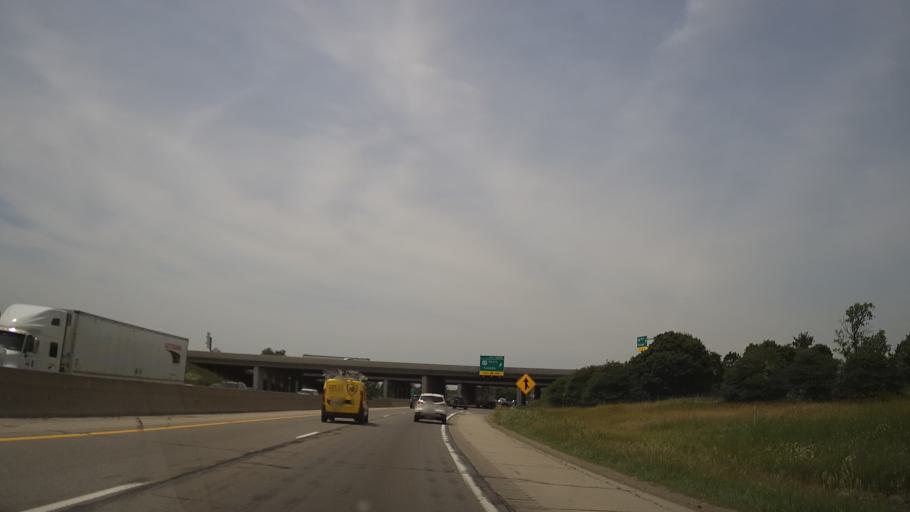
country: US
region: Michigan
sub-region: Washtenaw County
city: Ypsilanti
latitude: 42.2251
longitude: -83.6831
